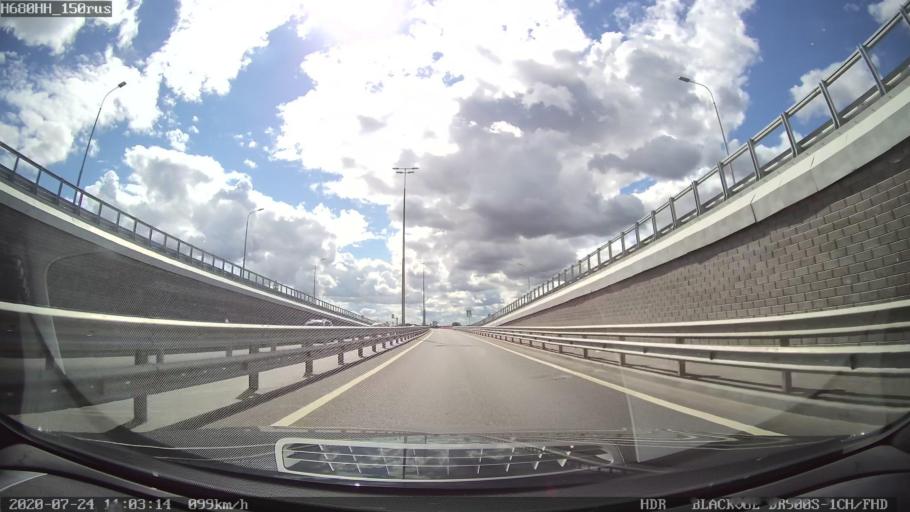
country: RU
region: St.-Petersburg
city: Shushary
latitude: 59.8055
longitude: 30.3340
